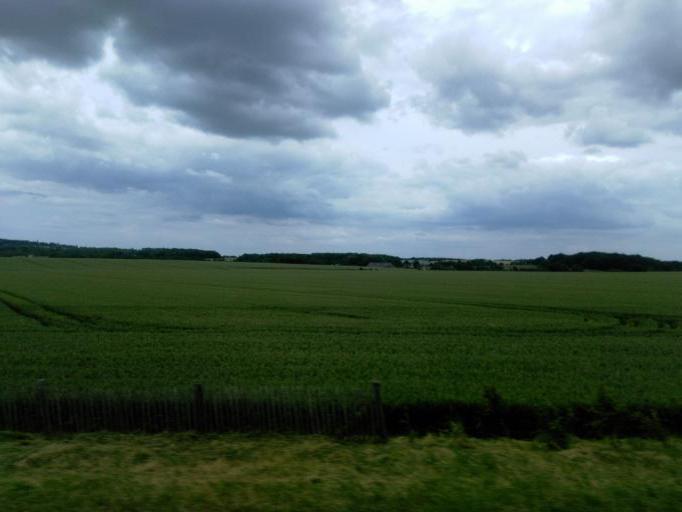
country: FR
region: Ile-de-France
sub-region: Departement du Val-d'Oise
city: Osny
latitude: 49.0978
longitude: 2.0475
